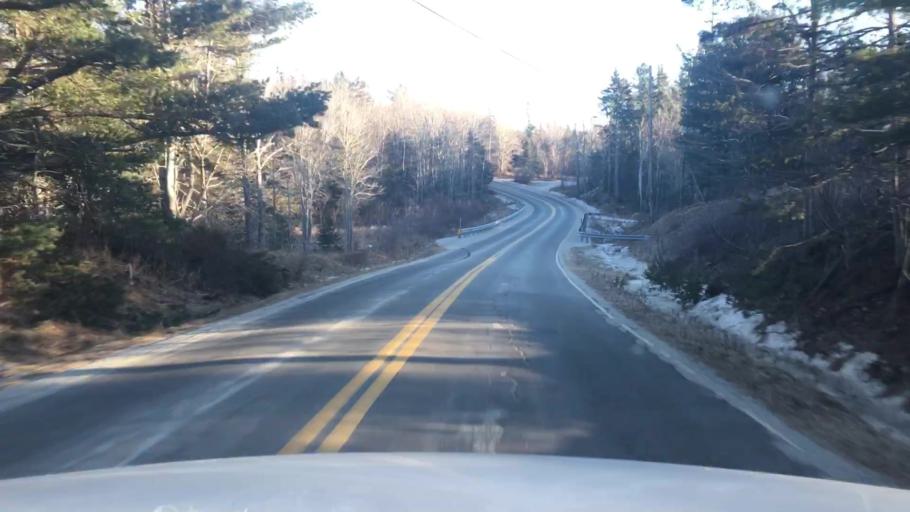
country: US
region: Maine
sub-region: Hancock County
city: Penobscot
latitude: 44.3880
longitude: -68.6977
